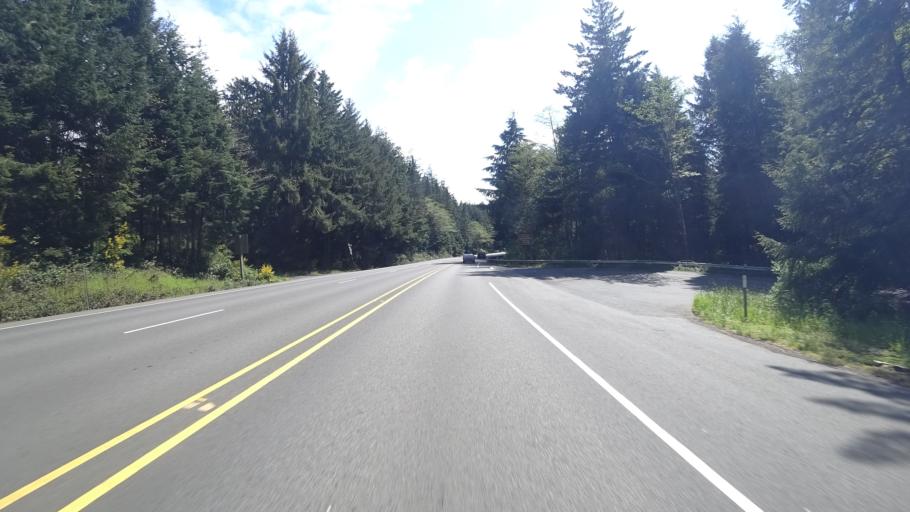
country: US
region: Oregon
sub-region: Lincoln County
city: Depoe Bay
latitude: 44.7491
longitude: -124.0514
